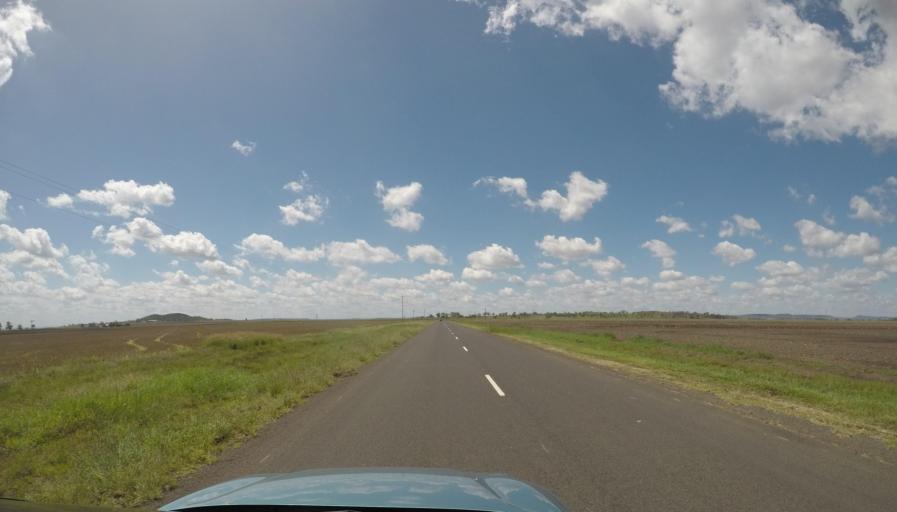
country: AU
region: Queensland
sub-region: Toowoomba
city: Oakey
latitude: -27.5279
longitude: 151.5736
